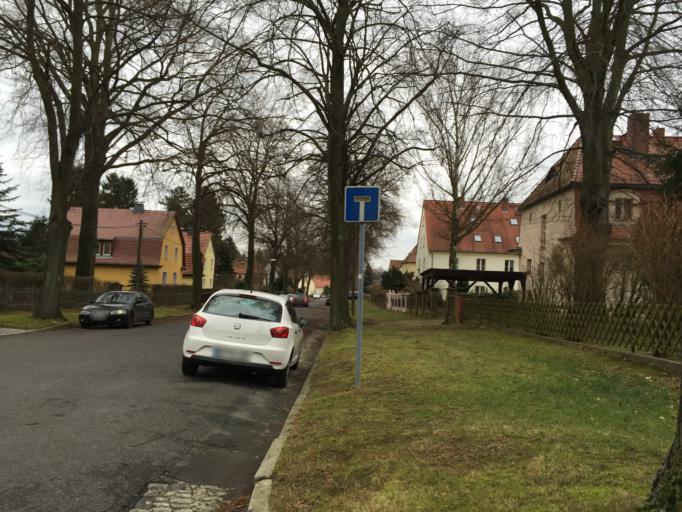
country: DE
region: Saxony
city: Goerlitz
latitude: 51.1399
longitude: 14.9653
